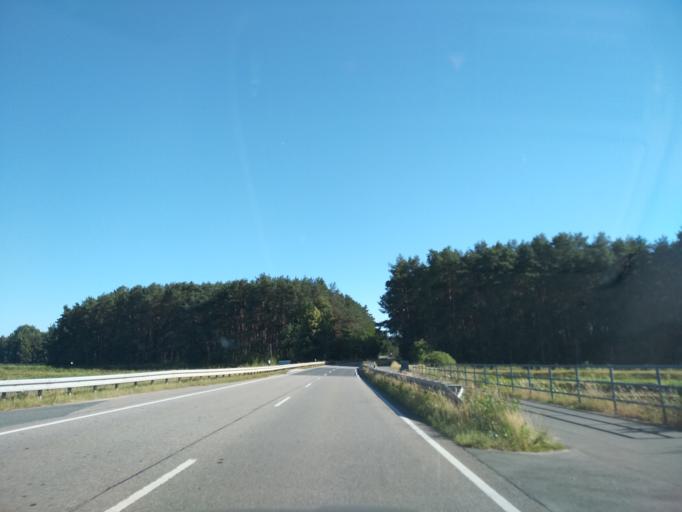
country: DE
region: Bavaria
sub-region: Regierungsbezirk Mittelfranken
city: Rottenbach
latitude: 49.6563
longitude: 10.9178
